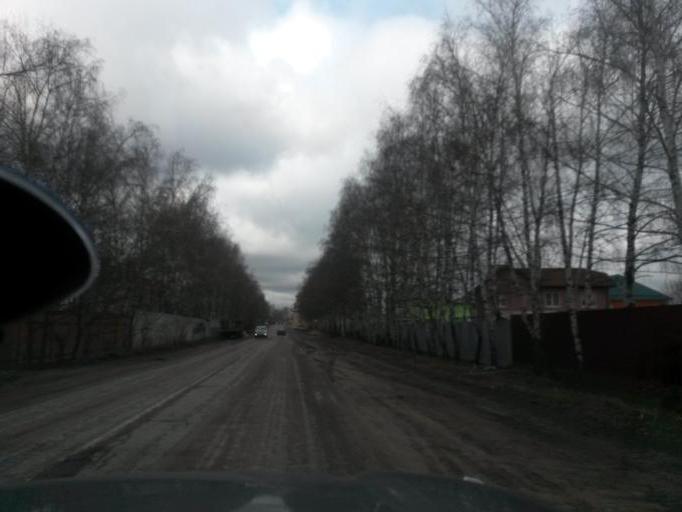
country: RU
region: Moskovskaya
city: Alekseyevka
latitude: 55.6024
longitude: 37.8110
